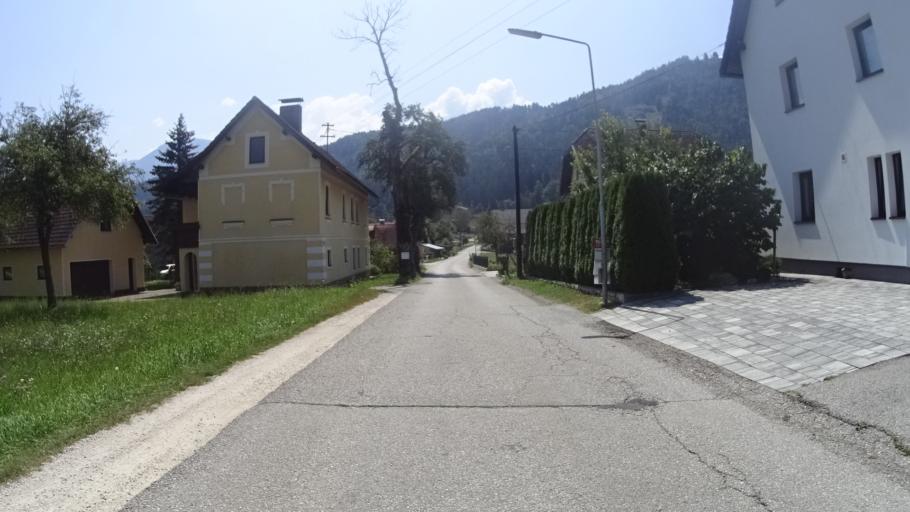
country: AT
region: Carinthia
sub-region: Politischer Bezirk Volkermarkt
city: Globasnitz
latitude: 46.5624
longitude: 14.6698
